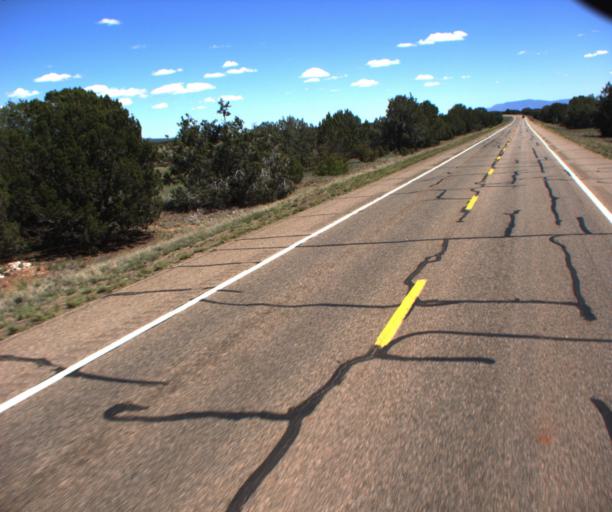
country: US
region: Arizona
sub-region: Yavapai County
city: Paulden
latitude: 35.1029
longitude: -112.4261
